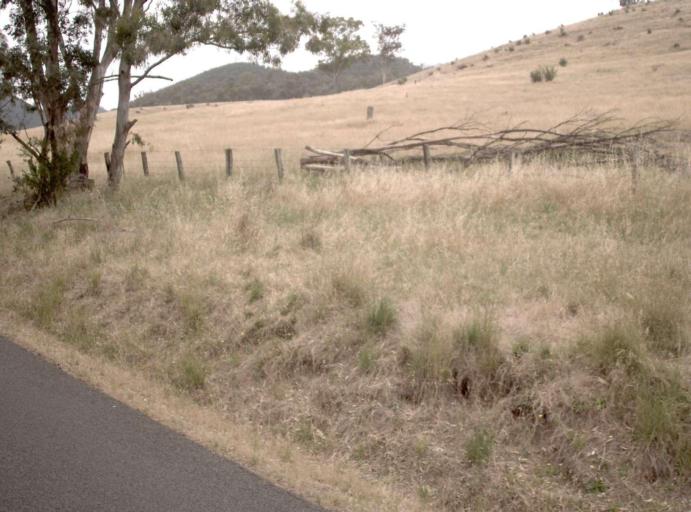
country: AU
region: Victoria
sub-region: Wellington
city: Heyfield
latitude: -37.6764
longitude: 146.6551
